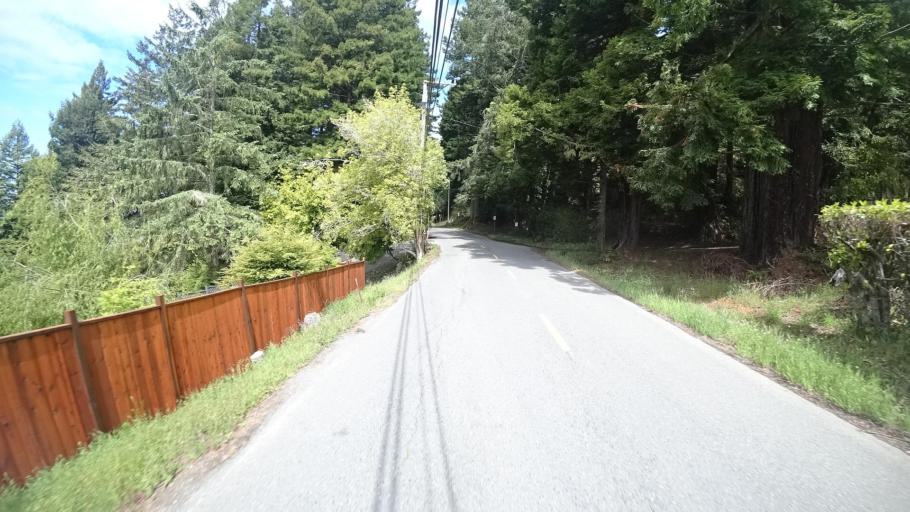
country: US
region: California
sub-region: Humboldt County
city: Bayside
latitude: 40.8679
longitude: -124.0559
